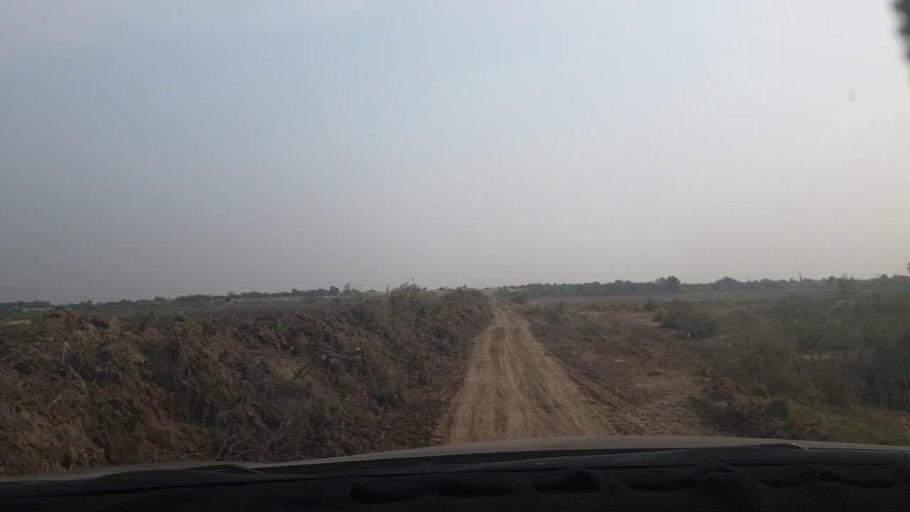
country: PK
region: Sindh
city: Jamshoro
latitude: 25.5204
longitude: 68.3213
